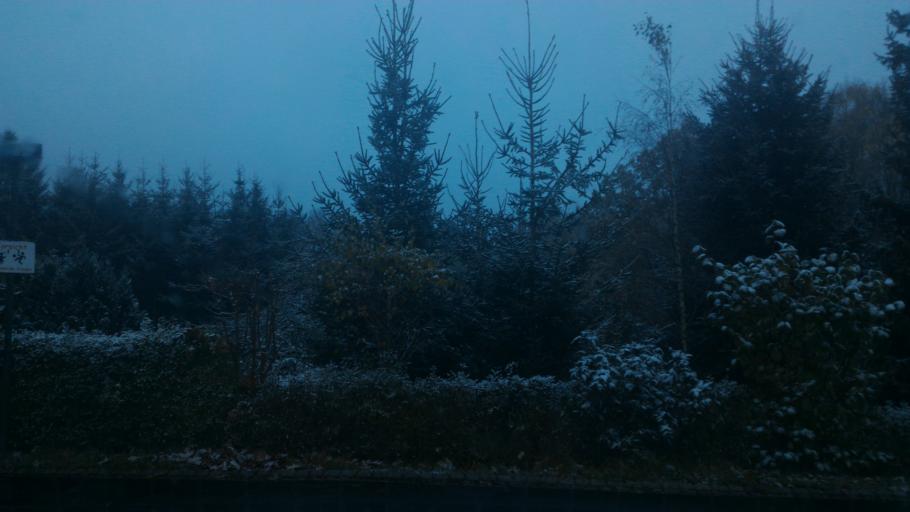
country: DE
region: Saxony
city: Friedersdorf
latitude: 51.0124
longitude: 14.5676
